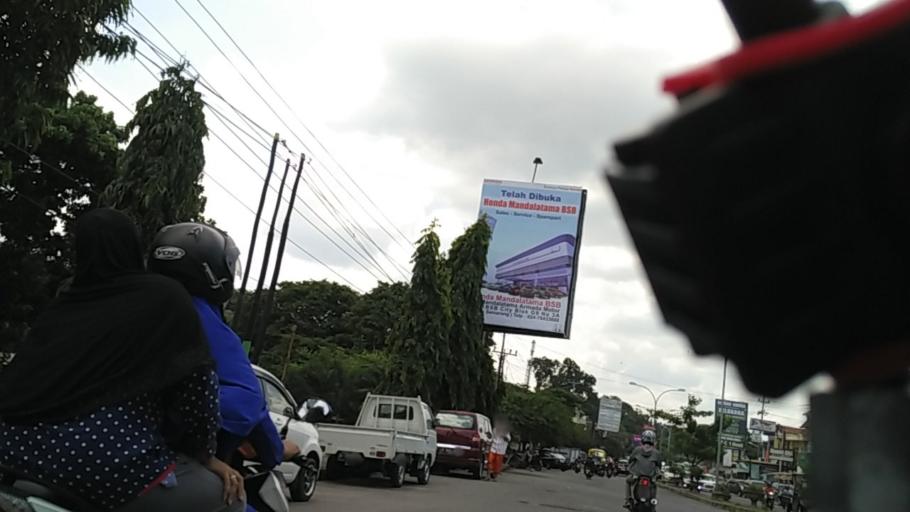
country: ID
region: Central Java
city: Semarang
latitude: -6.9968
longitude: 110.3469
